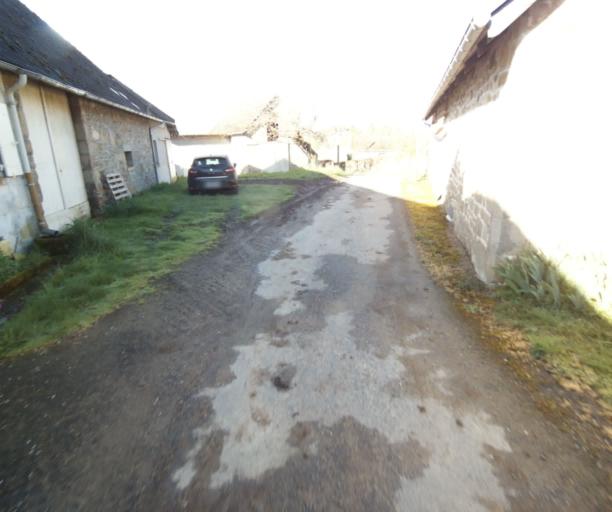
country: FR
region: Limousin
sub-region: Departement de la Correze
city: Laguenne
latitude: 45.2751
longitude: 1.8557
